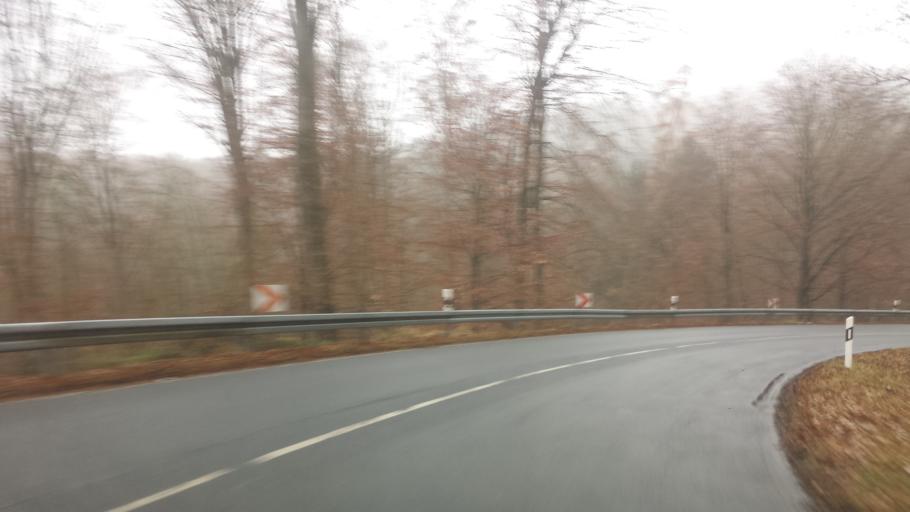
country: DE
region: Hesse
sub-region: Regierungsbezirk Darmstadt
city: Seeheim-Jugenheim
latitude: 49.7701
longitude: 8.6791
